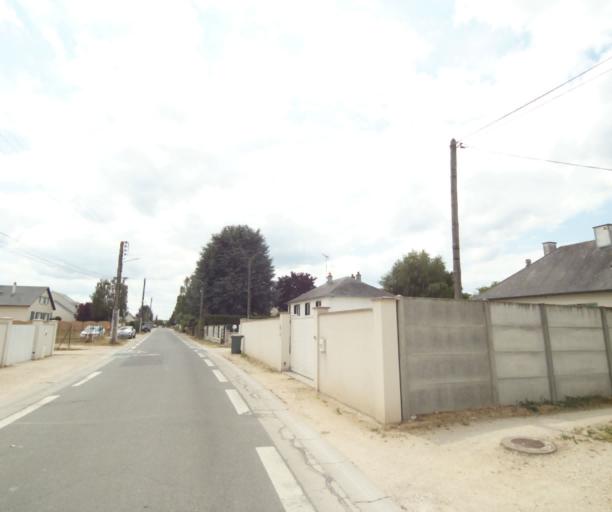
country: FR
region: Centre
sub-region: Departement du Loiret
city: Saint-Hilaire-Saint-Mesmin
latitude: 47.8628
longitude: 1.8461
